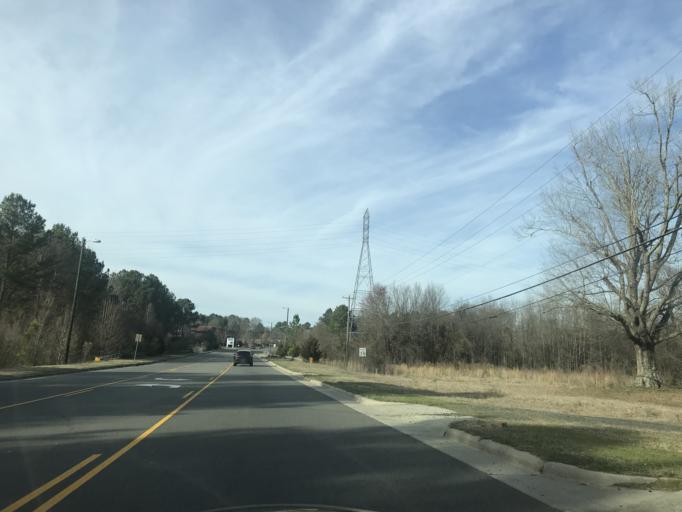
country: US
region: North Carolina
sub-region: Durham County
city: Durham
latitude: 35.9089
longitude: -78.8883
